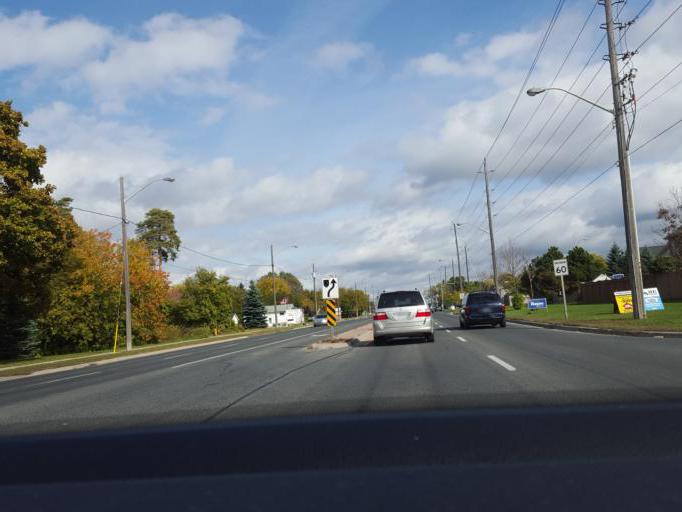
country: CA
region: Ontario
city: Oshawa
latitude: 43.9233
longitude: -78.9213
